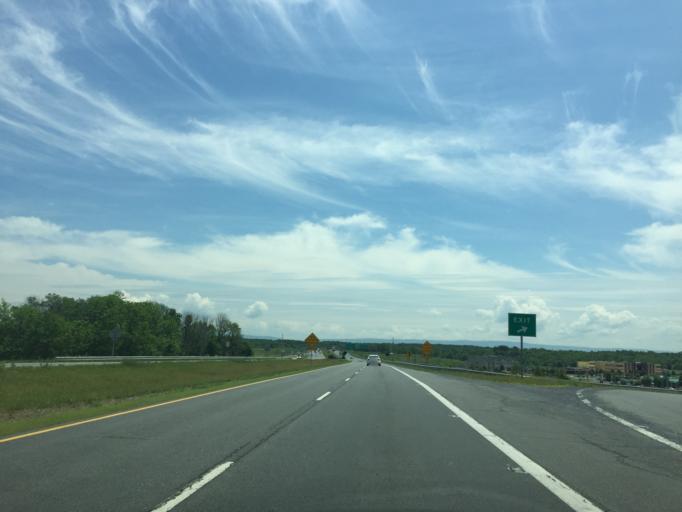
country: US
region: Virginia
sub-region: Frederick County
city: Stephens City
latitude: 39.1240
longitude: -78.1981
